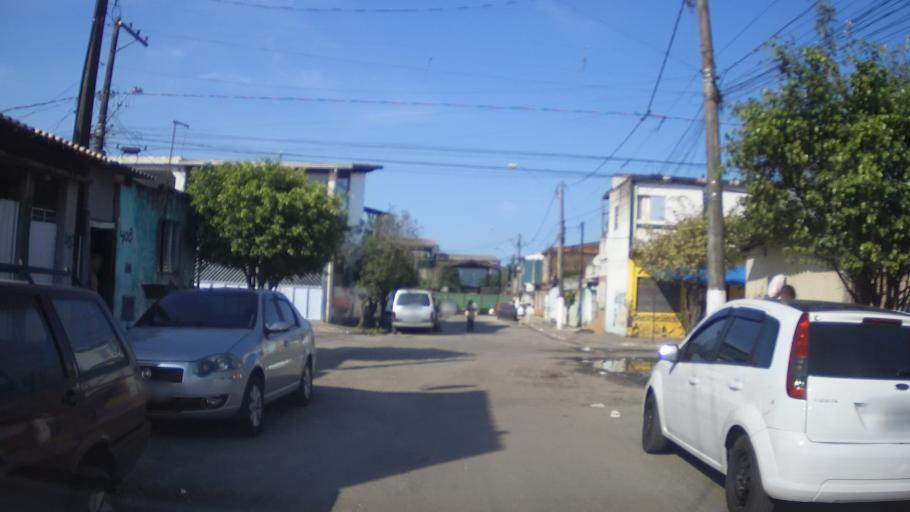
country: BR
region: Sao Paulo
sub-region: Praia Grande
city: Praia Grande
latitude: -24.0039
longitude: -46.4382
